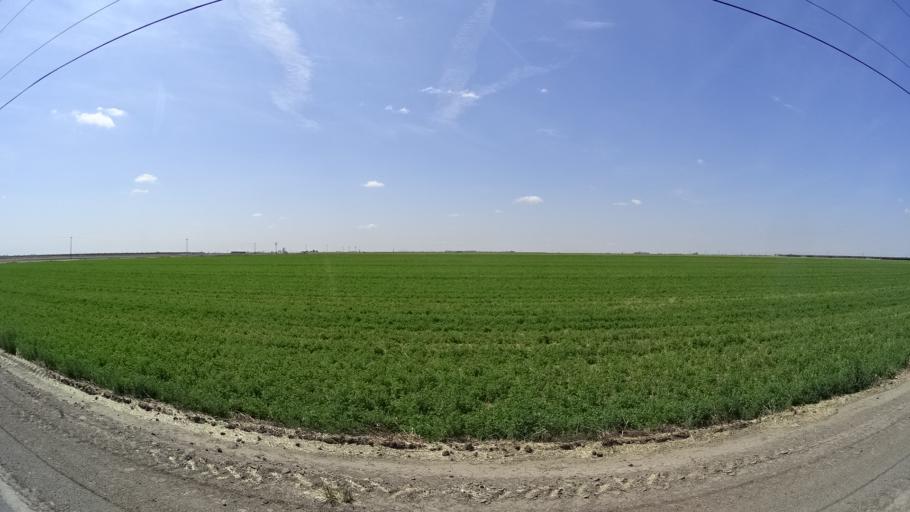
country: US
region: California
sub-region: Kings County
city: Home Garden
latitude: 36.2695
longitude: -119.5217
